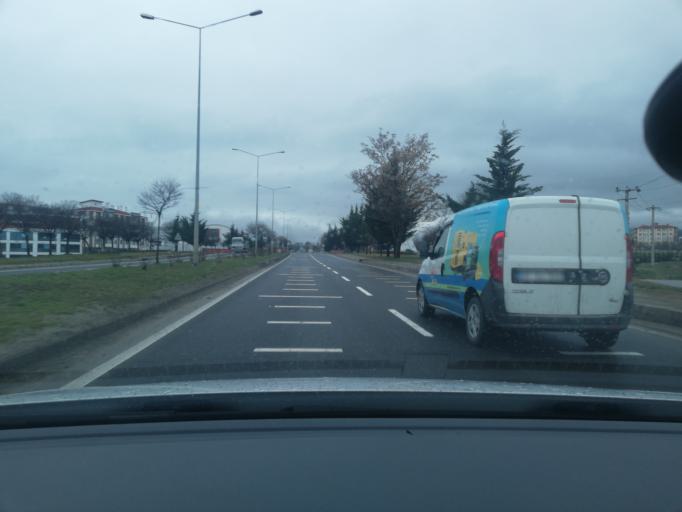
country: TR
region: Bolu
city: Bolu
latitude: 40.7359
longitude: 31.5884
